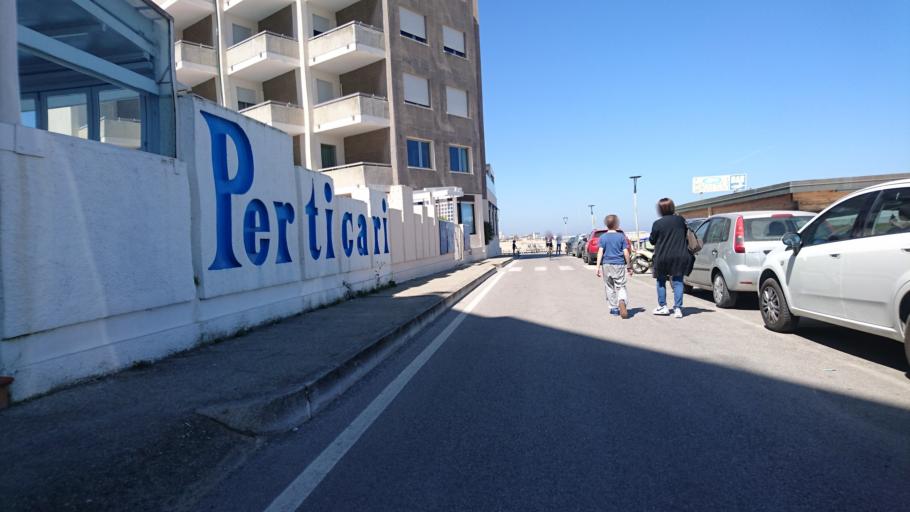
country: IT
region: The Marches
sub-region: Provincia di Pesaro e Urbino
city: Pesaro
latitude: 43.9155
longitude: 12.9167
